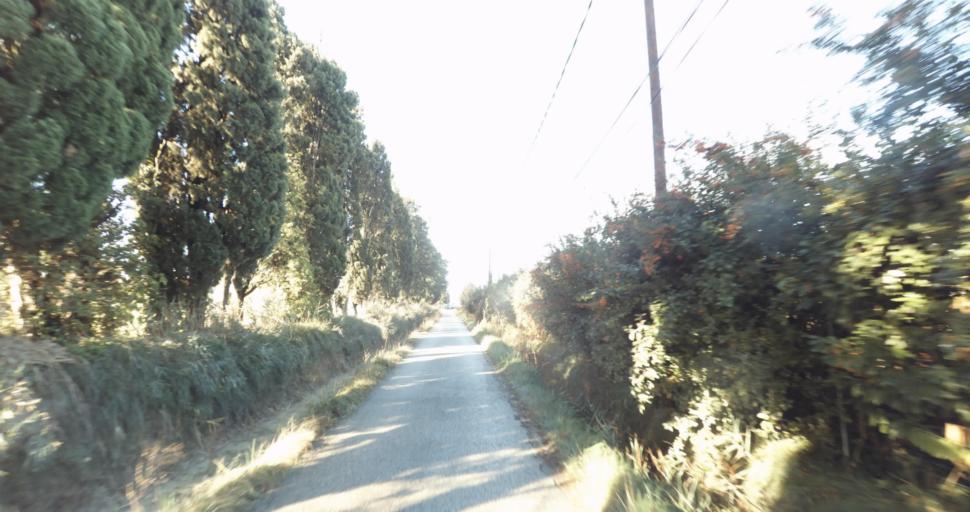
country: FR
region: Provence-Alpes-Cote d'Azur
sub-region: Departement des Bouches-du-Rhone
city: Rognonas
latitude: 43.8837
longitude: 4.7957
